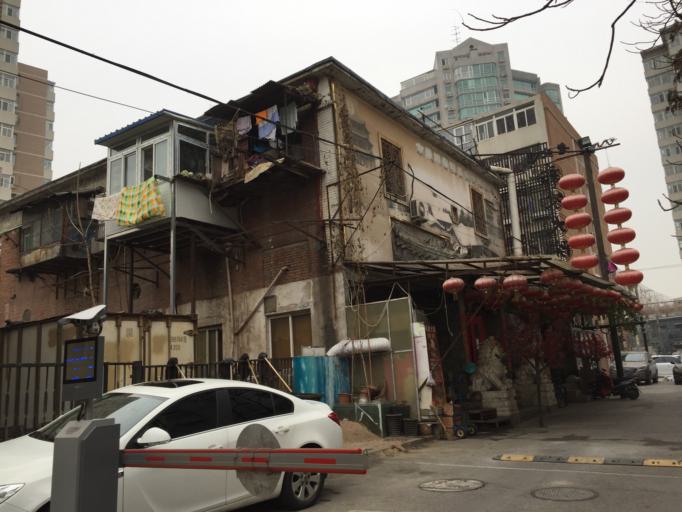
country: CN
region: Beijing
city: Chaowai
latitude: 39.9460
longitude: 116.4465
